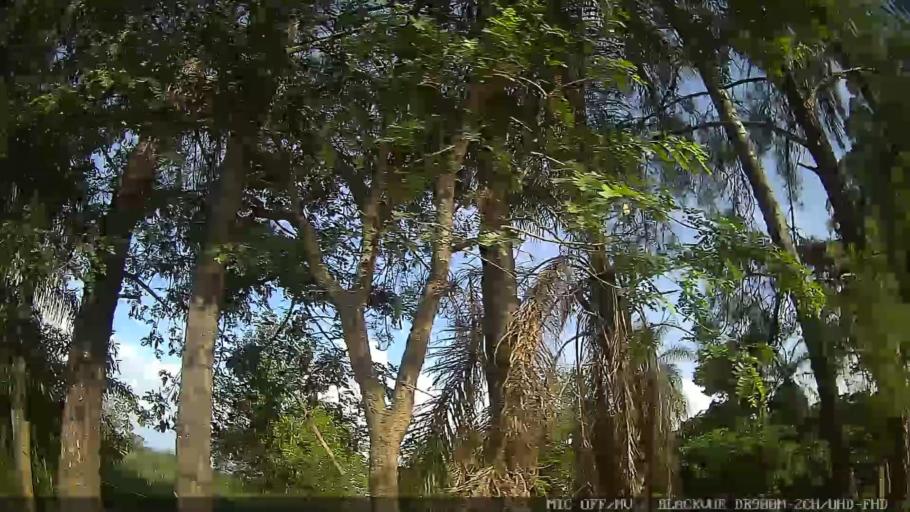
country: BR
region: Sao Paulo
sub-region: Jaguariuna
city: Jaguariuna
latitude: -22.6574
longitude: -47.0410
